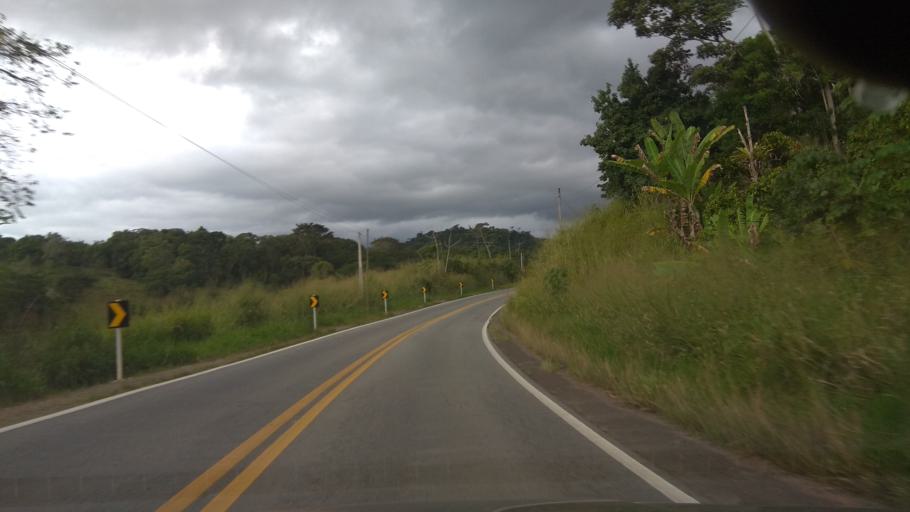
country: BR
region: Bahia
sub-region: Ubata
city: Ubata
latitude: -14.1931
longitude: -39.5604
